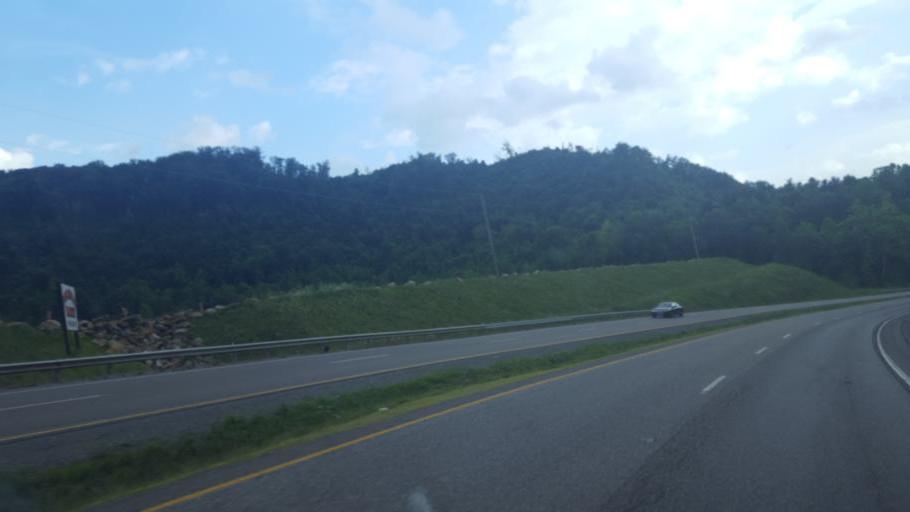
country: US
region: Virginia
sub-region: Wise County
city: Wise
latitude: 37.0087
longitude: -82.5896
